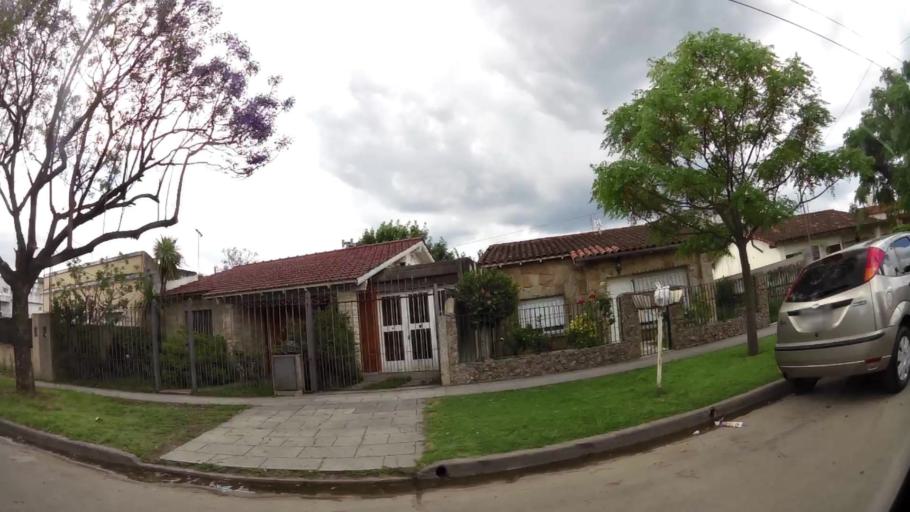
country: AR
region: Buenos Aires
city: Ituzaingo
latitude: -34.6423
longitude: -58.6851
